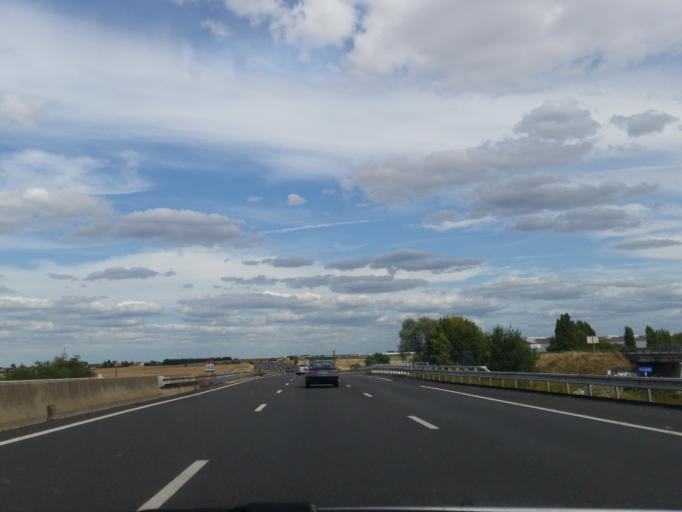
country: FR
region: Centre
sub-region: Departement du Loir-et-Cher
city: Villebarou
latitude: 47.6160
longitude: 1.3059
